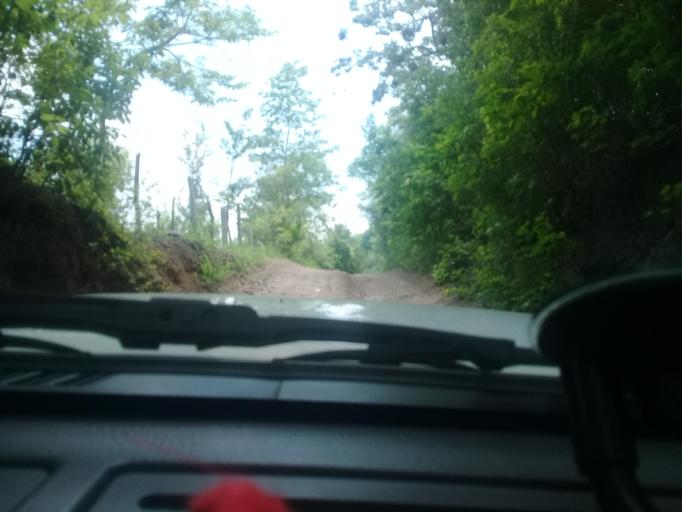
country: MX
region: Veracruz
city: Paso de Ovejas
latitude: 19.2844
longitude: -96.4282
